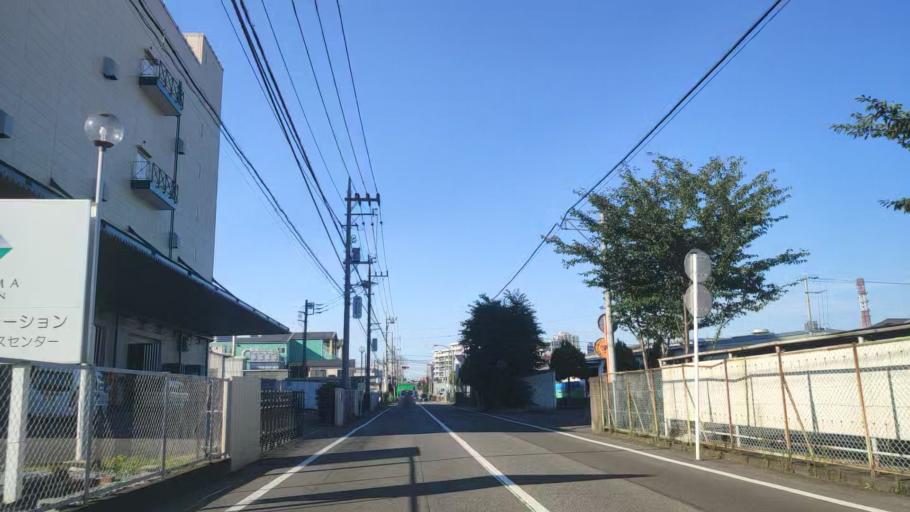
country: JP
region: Tokyo
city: Hachioji
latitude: 35.5872
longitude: 139.3335
